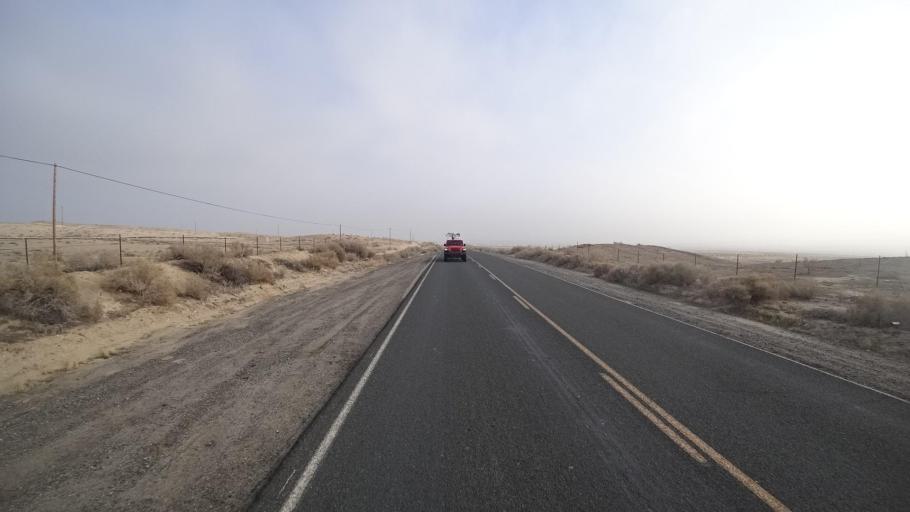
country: US
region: California
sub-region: Kern County
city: Ford City
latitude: 35.2416
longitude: -119.4532
